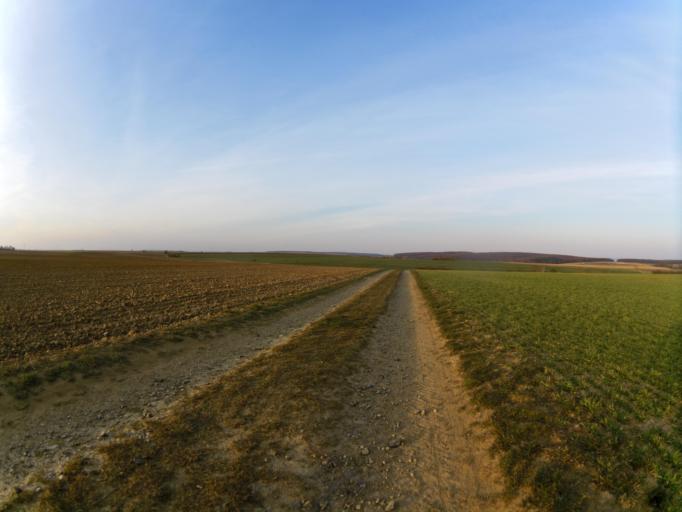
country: DE
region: Bavaria
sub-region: Regierungsbezirk Unterfranken
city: Prosselsheim
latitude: 49.8363
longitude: 10.1292
